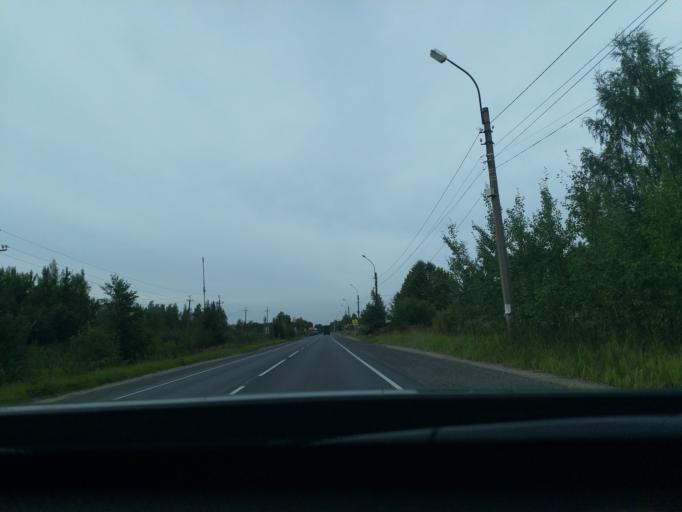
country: RU
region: Leningrad
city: Nikol'skoye
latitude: 59.7246
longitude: 30.7781
